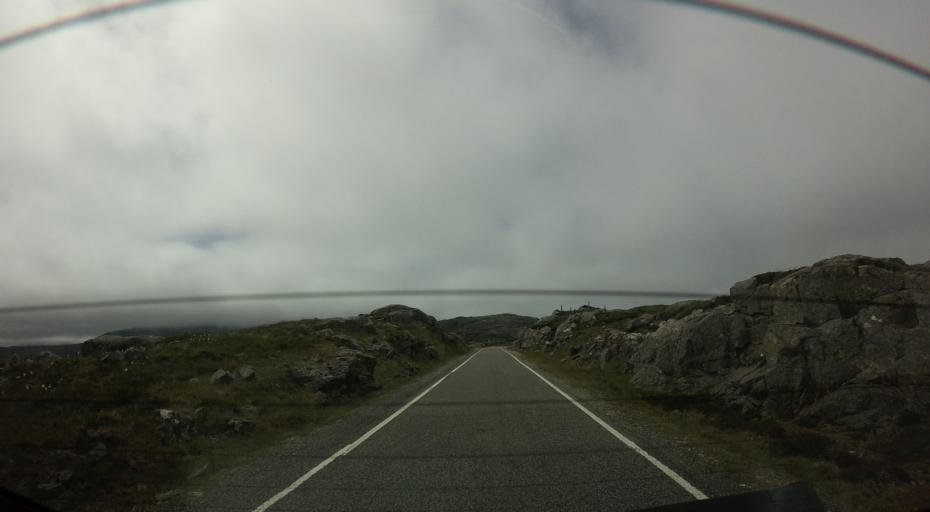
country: GB
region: Scotland
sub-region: Eilean Siar
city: Harris
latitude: 57.8489
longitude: -6.8400
